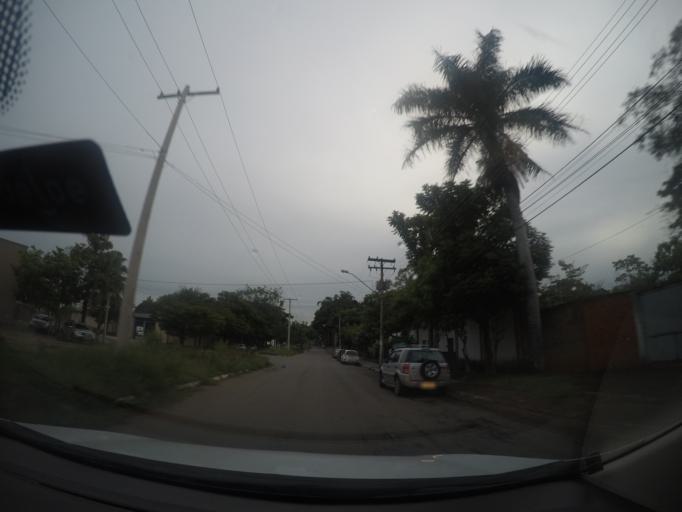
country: BR
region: Goias
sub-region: Goiania
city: Goiania
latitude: -16.6372
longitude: -49.2444
